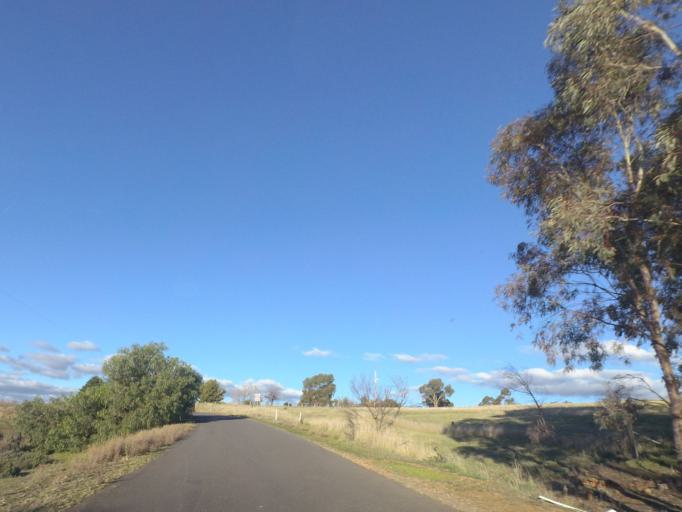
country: AU
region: Victoria
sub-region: Mount Alexander
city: Castlemaine
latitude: -37.1590
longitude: 144.2159
